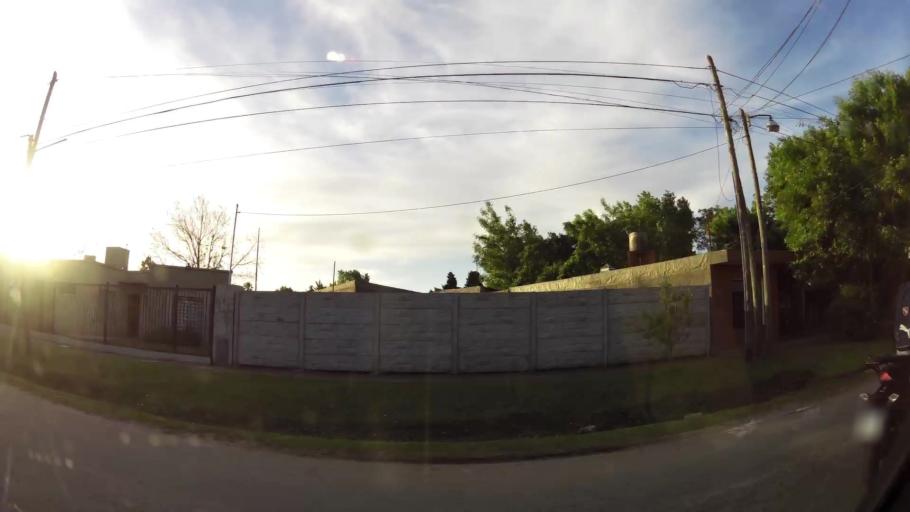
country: AR
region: Buenos Aires
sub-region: Partido de Quilmes
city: Quilmes
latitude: -34.7875
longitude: -58.1886
